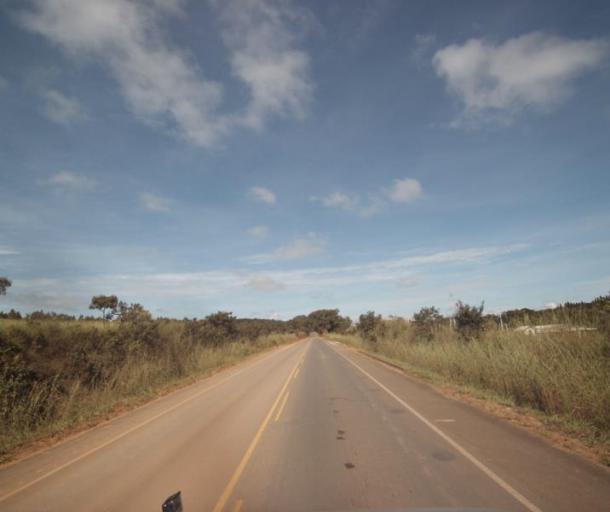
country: BR
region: Goias
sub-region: Anapolis
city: Anapolis
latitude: -16.1623
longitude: -48.8915
